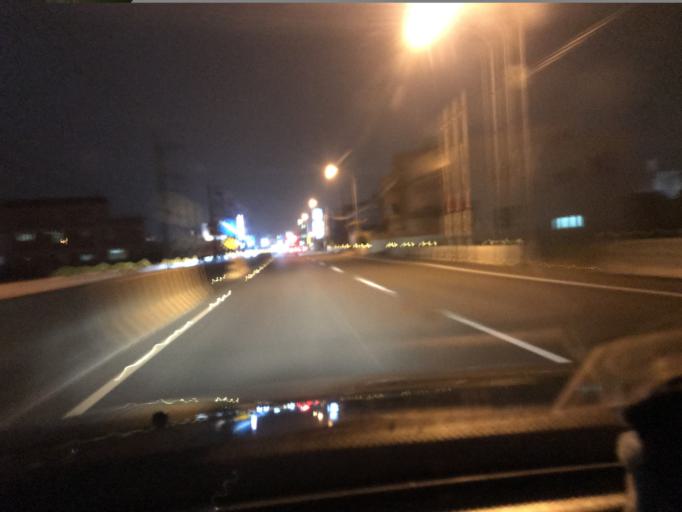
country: TW
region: Taiwan
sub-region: Hsinchu
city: Zhubei
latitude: 24.7770
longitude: 121.0719
